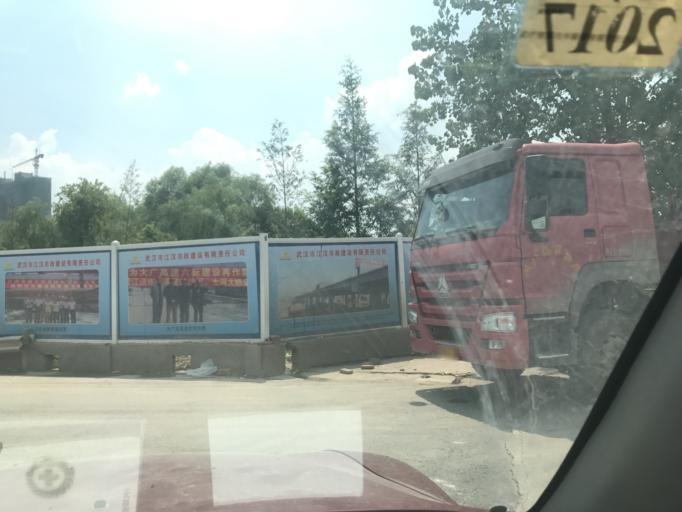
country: CN
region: Hubei
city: Shekou
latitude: 30.6917
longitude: 114.3394
